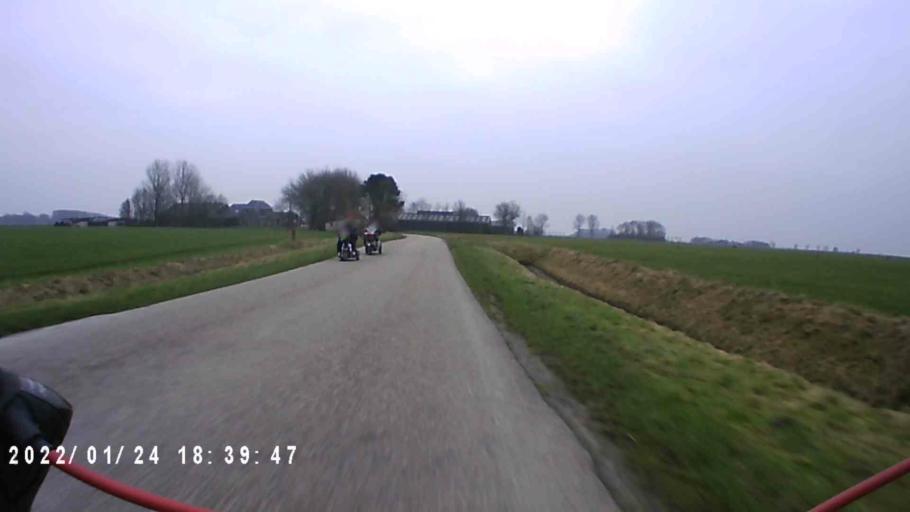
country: NL
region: Groningen
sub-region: Gemeente De Marne
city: Ulrum
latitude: 53.3469
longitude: 6.3419
